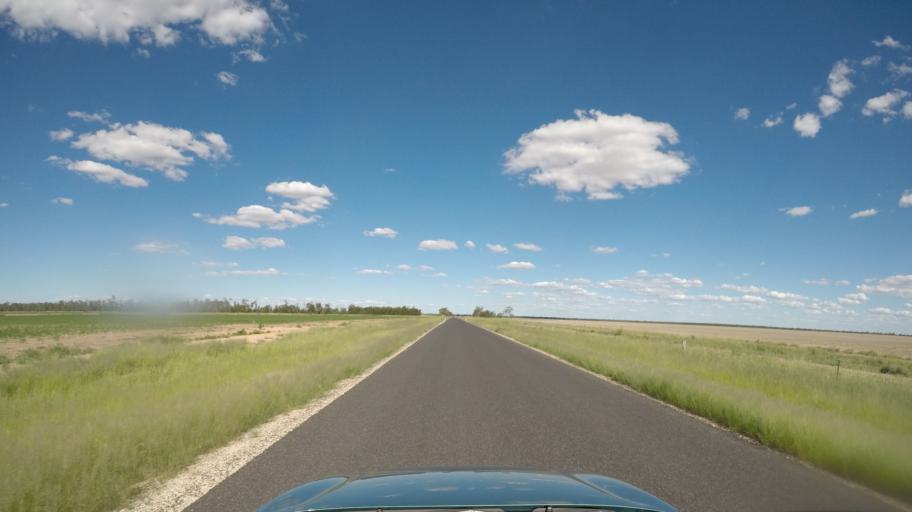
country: AU
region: Queensland
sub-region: Goondiwindi
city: Goondiwindi
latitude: -28.1752
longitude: 150.2512
